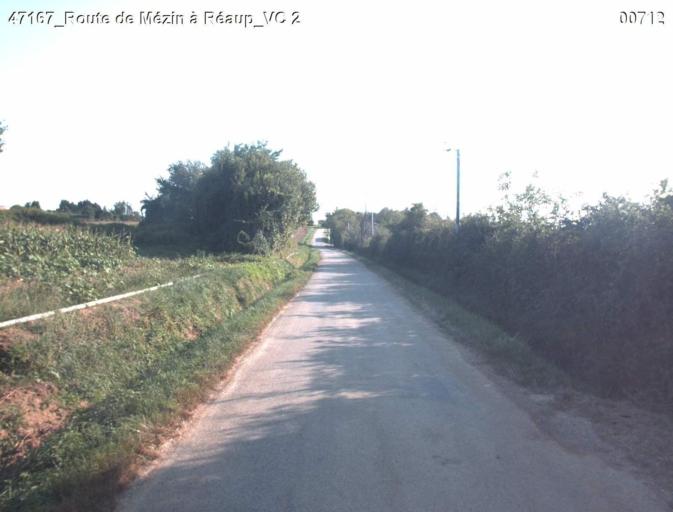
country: FR
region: Aquitaine
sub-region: Departement du Lot-et-Garonne
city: Mezin
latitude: 44.0639
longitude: 0.2568
